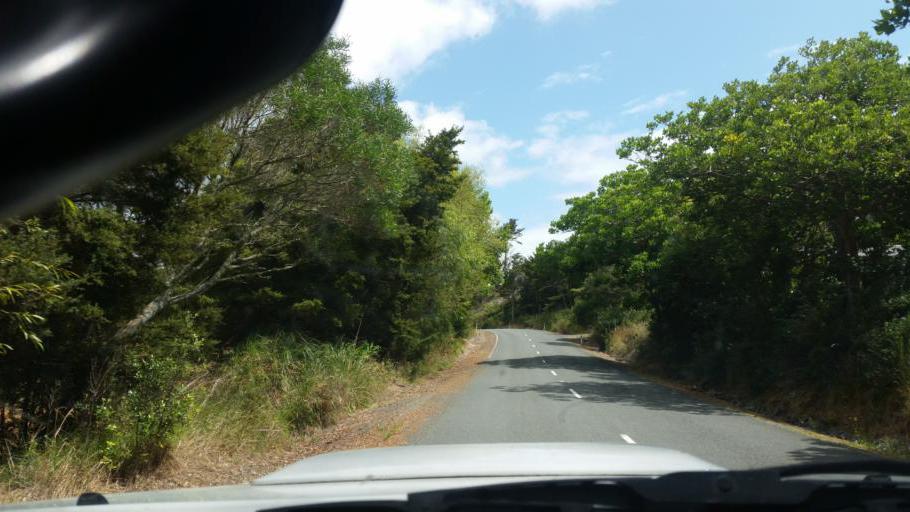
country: NZ
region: Auckland
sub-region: Auckland
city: Wellsford
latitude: -36.1427
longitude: 174.5577
